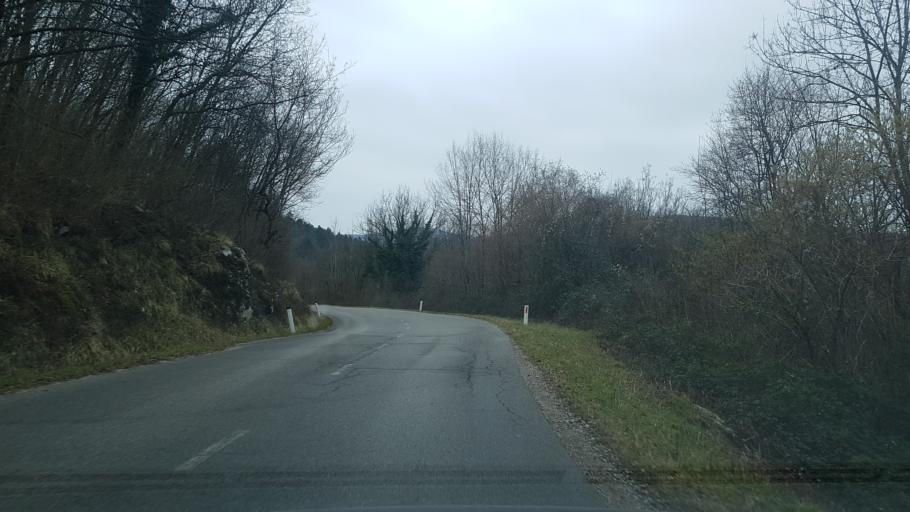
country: SI
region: Kanal
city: Kanal
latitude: 46.0396
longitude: 13.6721
